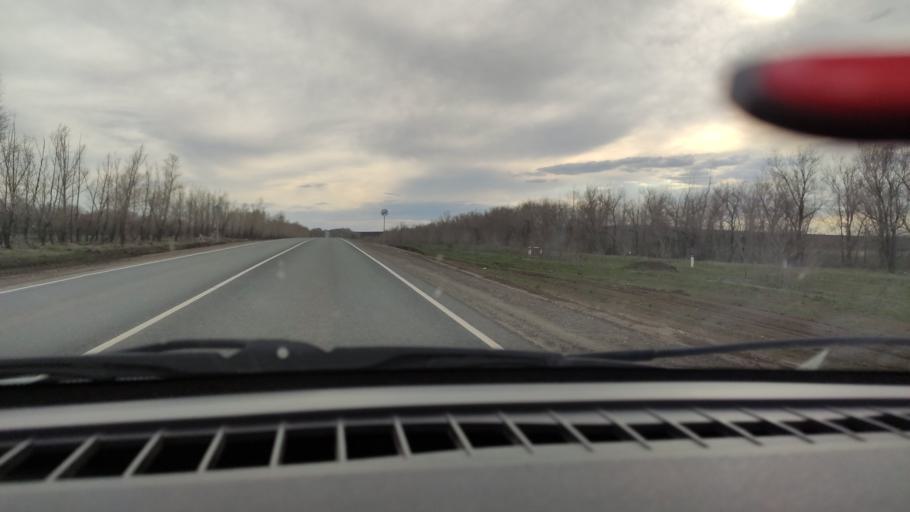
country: RU
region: Orenburg
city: Sakmara
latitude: 52.3176
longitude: 55.4718
